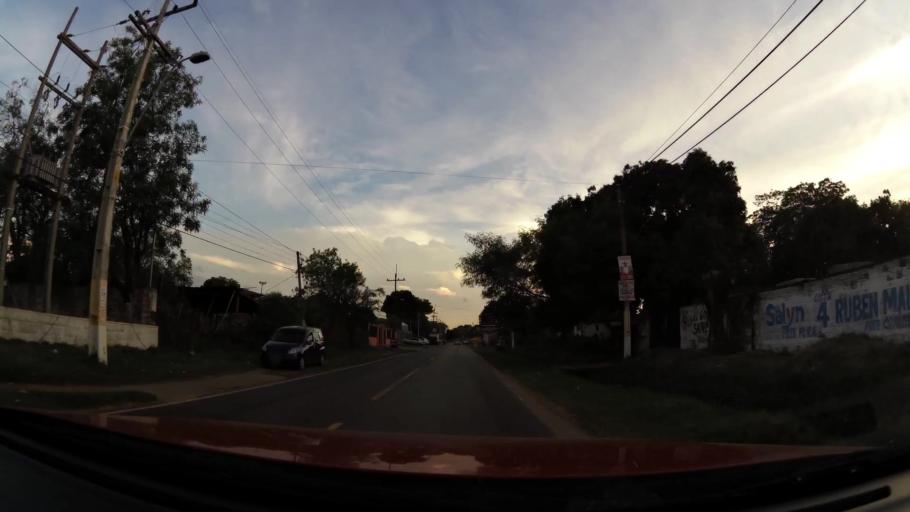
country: PY
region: Central
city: San Lorenzo
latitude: -25.3537
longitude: -57.4907
